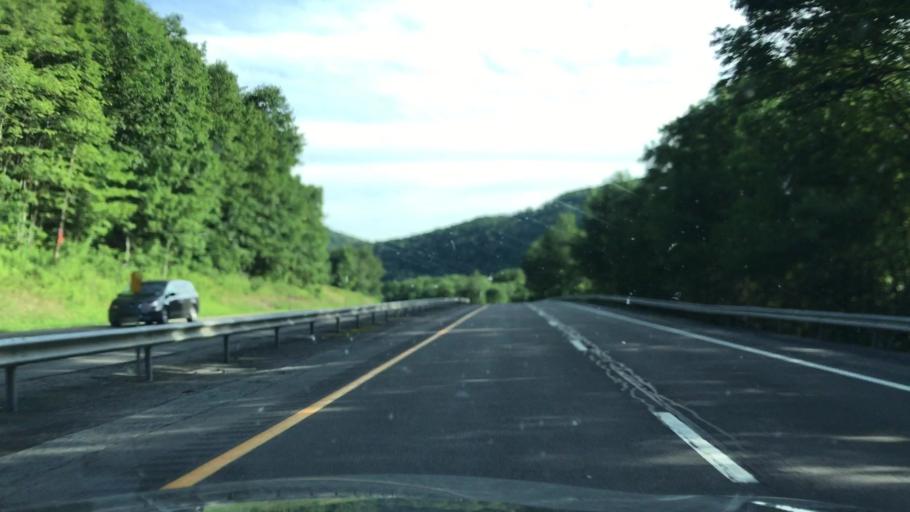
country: US
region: New York
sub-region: Delaware County
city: Hancock
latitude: 41.9820
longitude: -75.3374
